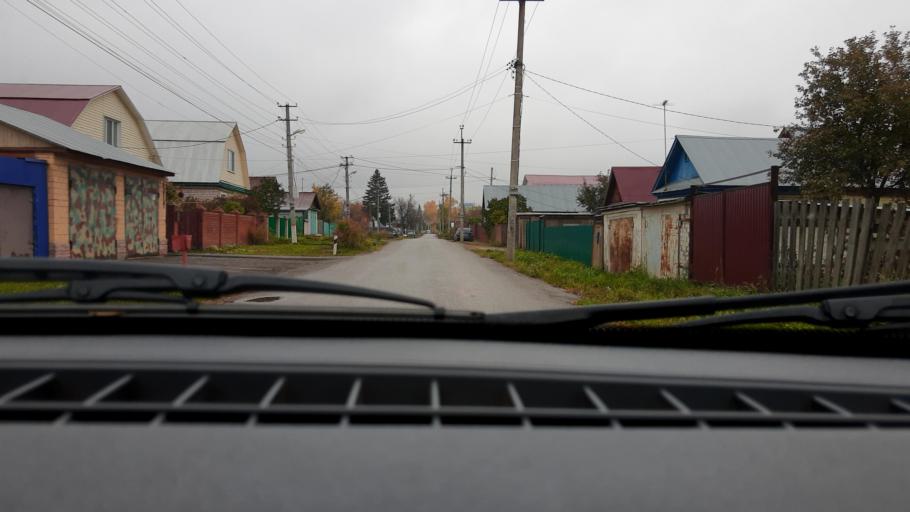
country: RU
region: Bashkortostan
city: Mikhaylovka
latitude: 54.7908
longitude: 55.8867
